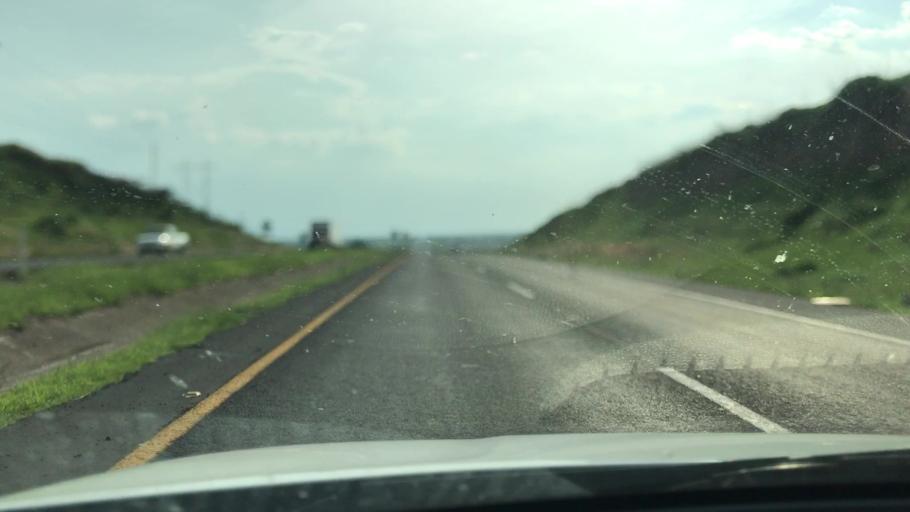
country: MX
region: Guanajuato
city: Penjamo
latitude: 20.3841
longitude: -101.7931
